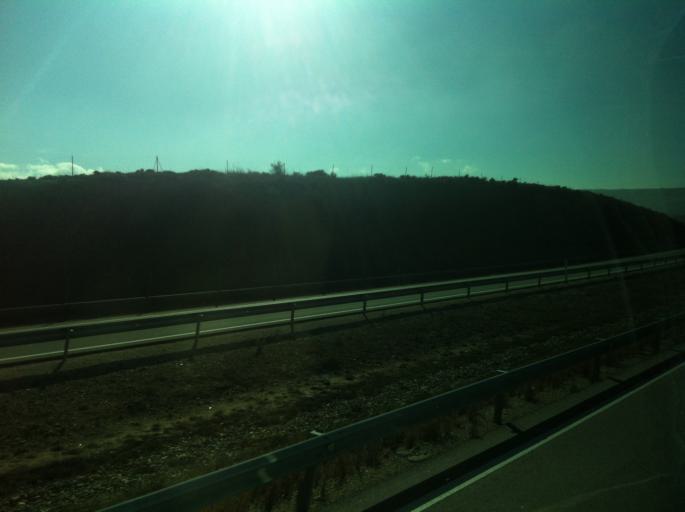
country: ES
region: Castille and Leon
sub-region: Provincia de Burgos
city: Quintanapalla
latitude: 42.4221
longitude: -3.5180
